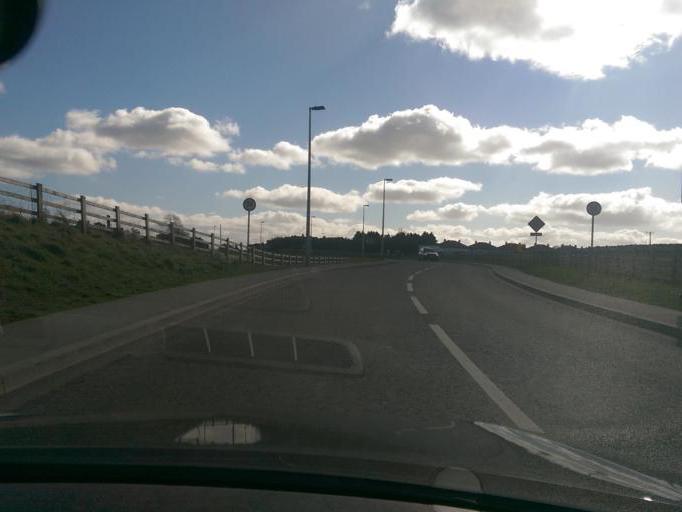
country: IE
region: Connaught
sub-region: County Galway
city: Athenry
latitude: 53.3101
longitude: -8.7544
